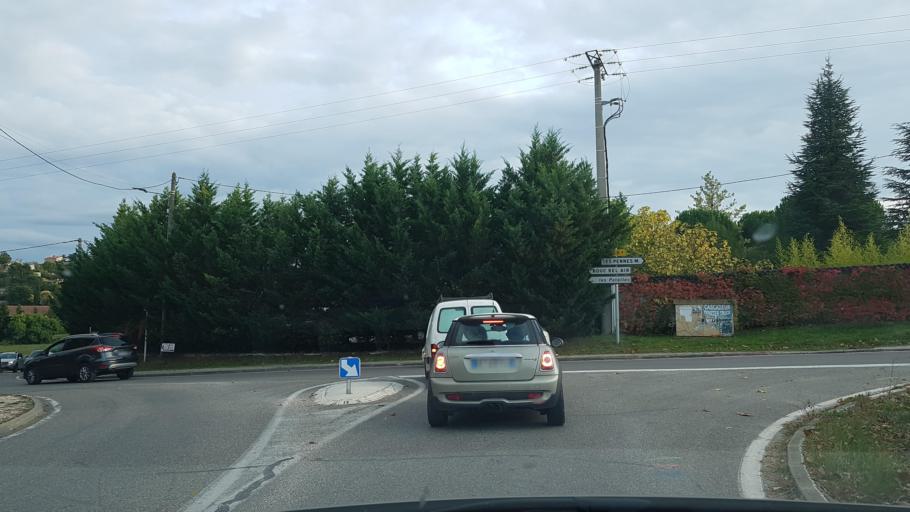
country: FR
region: Provence-Alpes-Cote d'Azur
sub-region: Departement des Bouches-du-Rhone
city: Cabries
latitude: 43.4450
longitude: 5.3720
